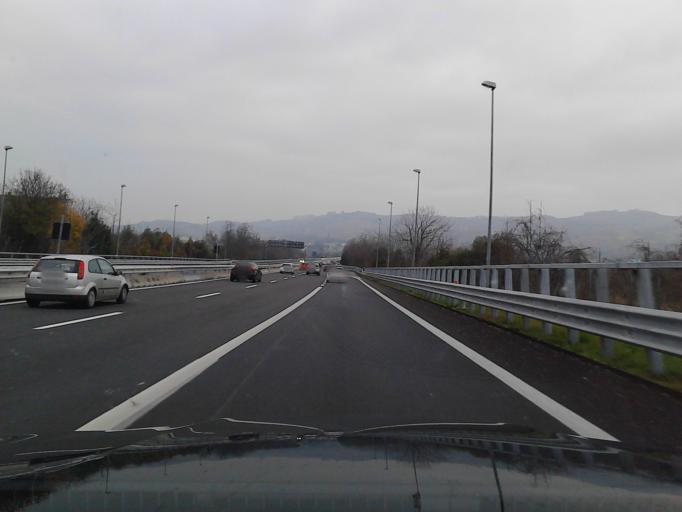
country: IT
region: Abruzzo
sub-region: Provincia di Teramo
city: Villa Rosa
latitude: 42.8361
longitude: 13.9041
